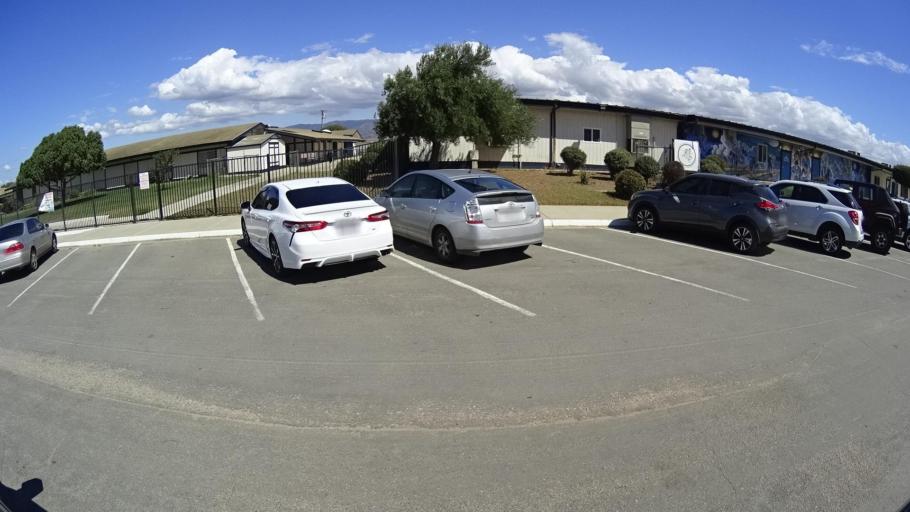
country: US
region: California
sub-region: Monterey County
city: Chualar
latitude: 36.5715
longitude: -121.5161
